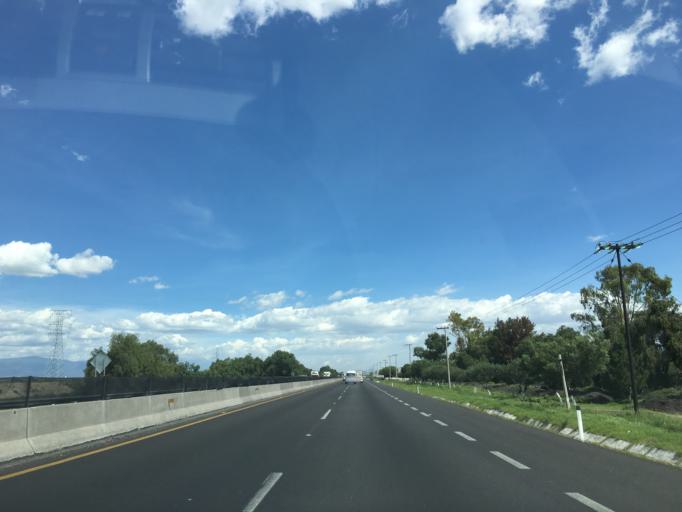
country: MX
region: Mexico
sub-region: Jaltenco
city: Alborada Jaltenco
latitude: 19.6625
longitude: -99.0649
